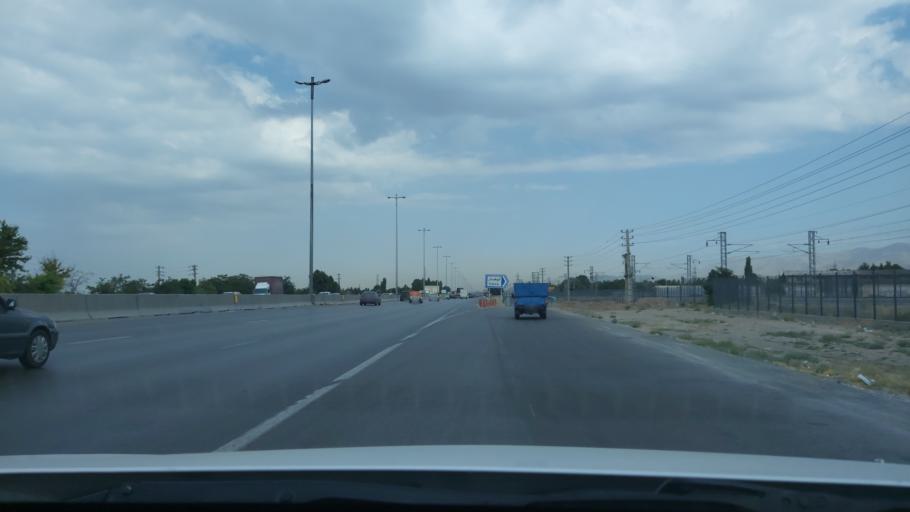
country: IR
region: Alborz
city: Hashtgerd
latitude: 35.9332
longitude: 50.7592
